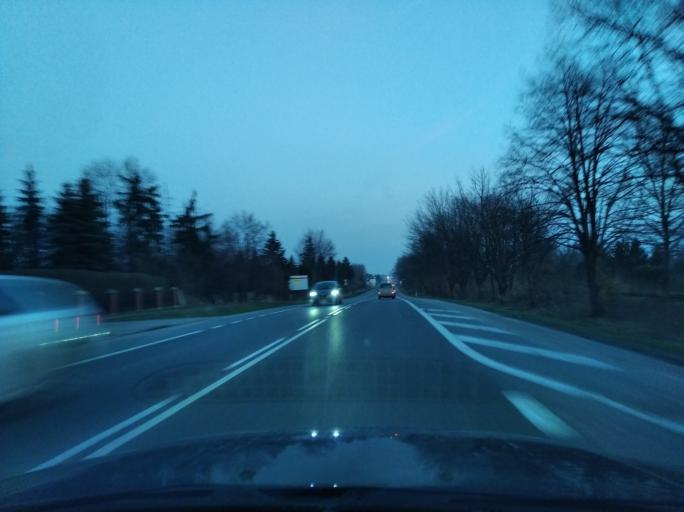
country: PL
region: Subcarpathian Voivodeship
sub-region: Powiat rzeszowski
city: Rudna Mala
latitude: 50.1020
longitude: 21.9776
